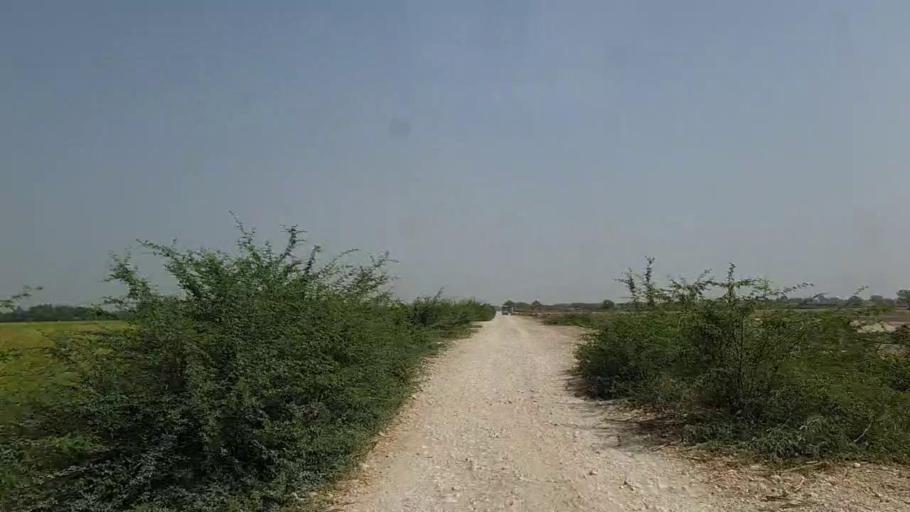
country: PK
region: Sindh
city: Naukot
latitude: 24.8125
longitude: 69.3794
